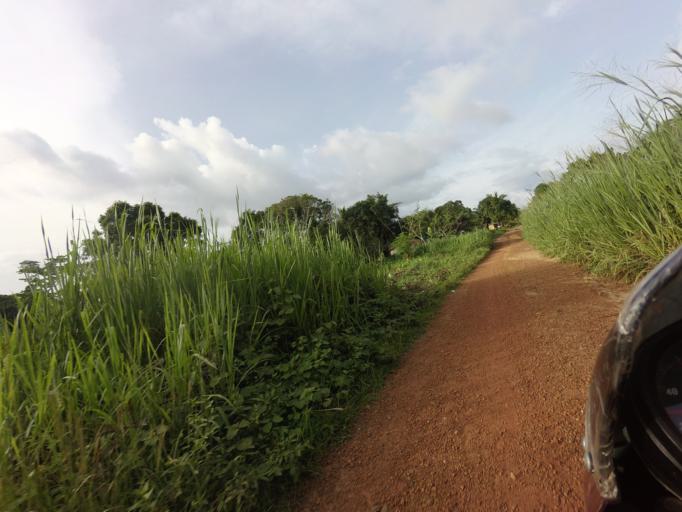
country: SL
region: Eastern Province
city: Jojoima
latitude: 7.8495
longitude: -10.8087
